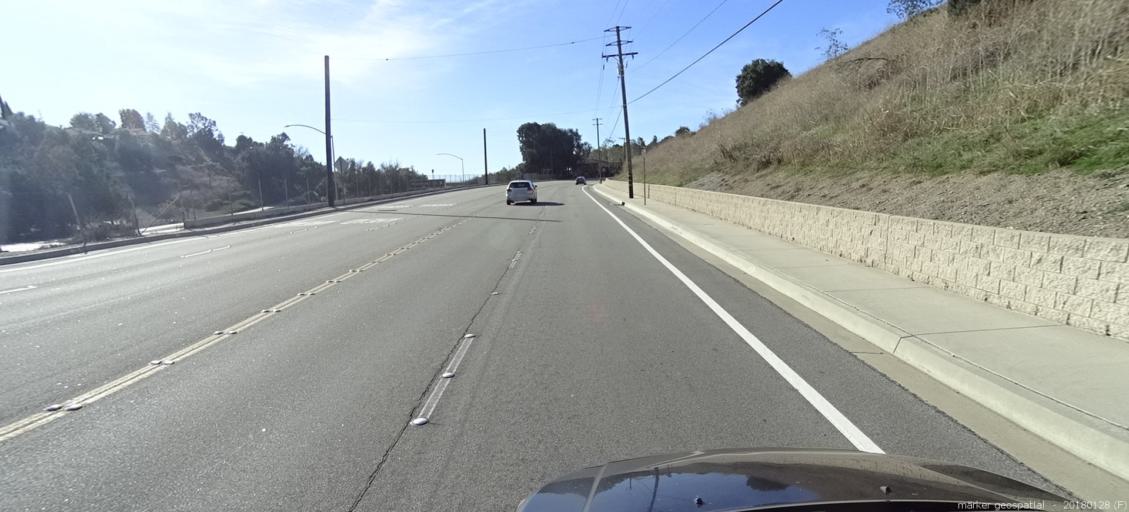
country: US
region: California
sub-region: Los Angeles County
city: Walnut
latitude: 33.9892
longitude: -117.8435
